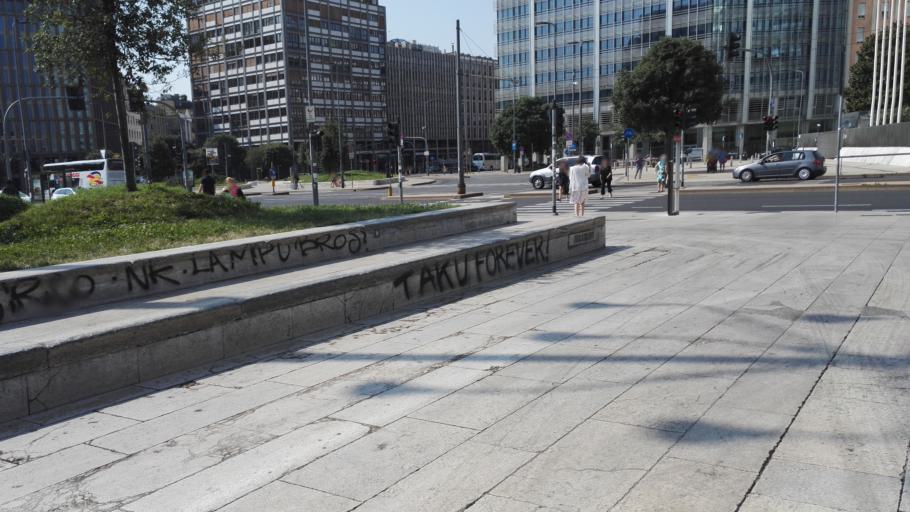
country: IT
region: Lombardy
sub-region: Citta metropolitana di Milano
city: Milano
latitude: 45.4851
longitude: 9.2020
